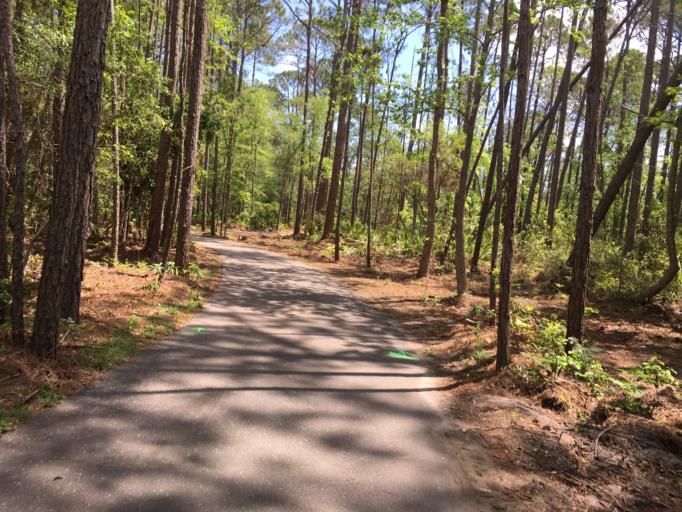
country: US
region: South Carolina
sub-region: Beaufort County
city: Hilton Head Island
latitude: 32.1686
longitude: -80.7692
